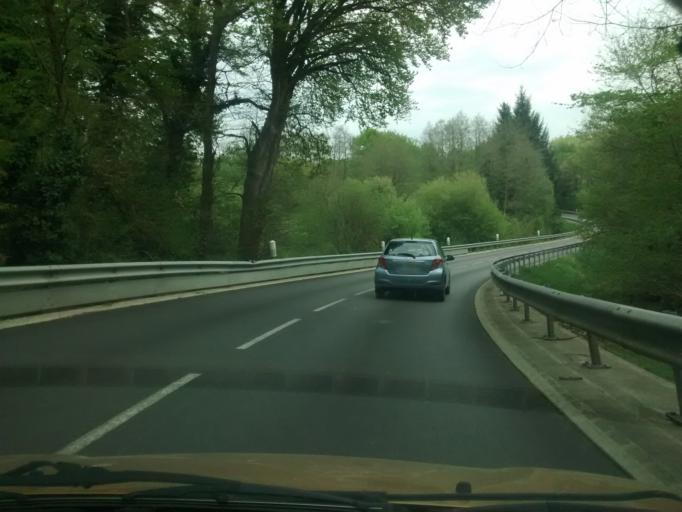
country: FR
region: Brittany
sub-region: Departement du Morbihan
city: Berric
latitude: 47.6431
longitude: -2.5094
